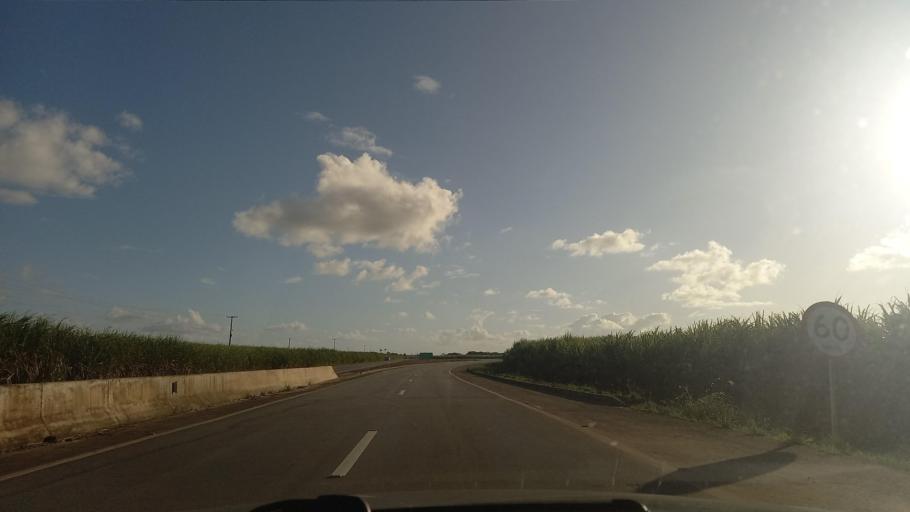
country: BR
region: Alagoas
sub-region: Sao Miguel Dos Campos
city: Sao Miguel dos Campos
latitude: -9.8012
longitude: -36.1934
